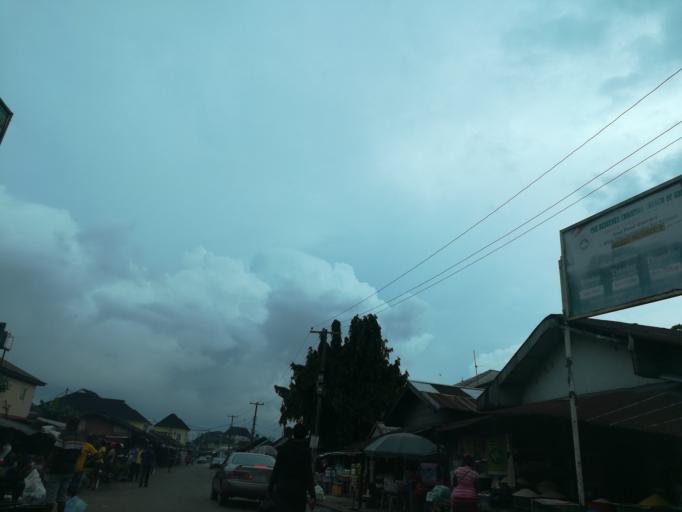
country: NG
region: Rivers
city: Port Harcourt
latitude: 4.8144
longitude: 7.0140
